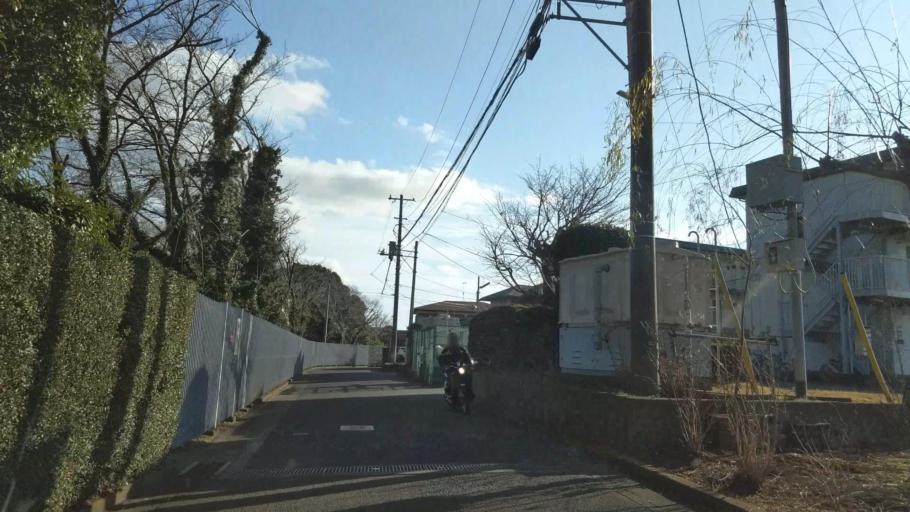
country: JP
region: Kanagawa
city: Isehara
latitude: 35.3651
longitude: 139.2706
